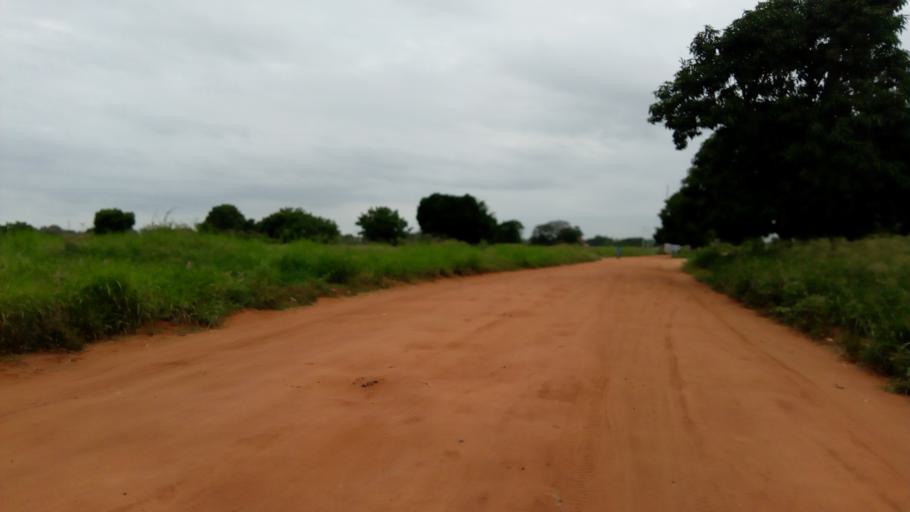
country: TG
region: Maritime
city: Lome
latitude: 6.1818
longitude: 1.2116
